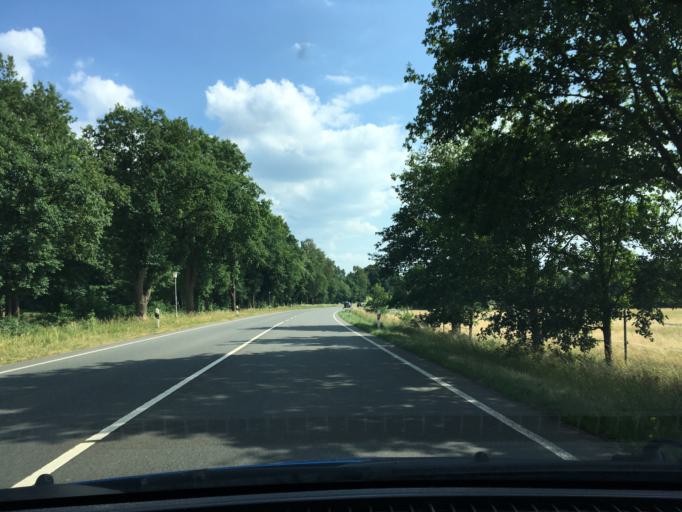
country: DE
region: Lower Saxony
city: Welle
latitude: 53.2520
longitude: 9.8082
